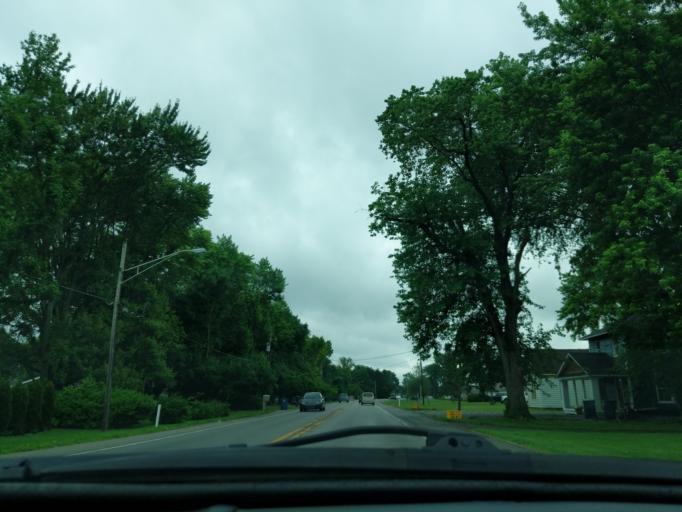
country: US
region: Indiana
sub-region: Hamilton County
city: Noblesville
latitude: 40.0523
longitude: -86.0303
